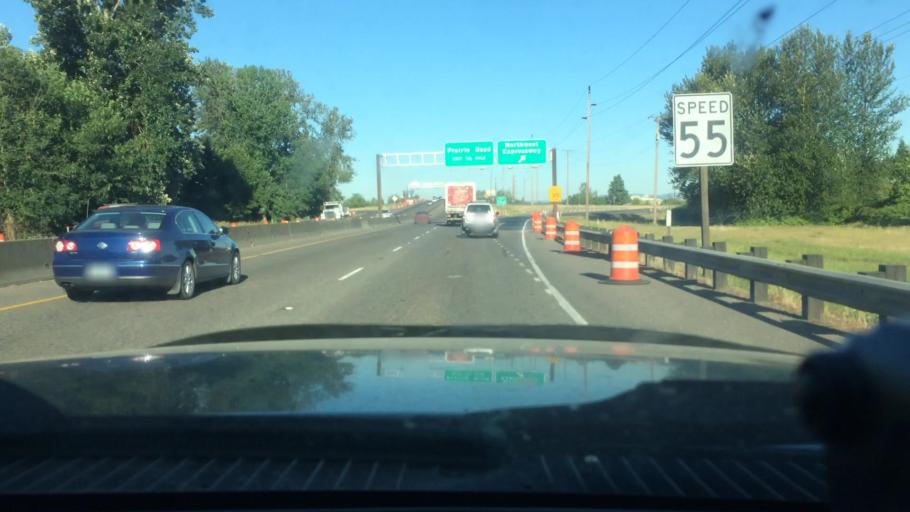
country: US
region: Oregon
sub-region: Lane County
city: Eugene
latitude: 44.0980
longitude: -123.1496
